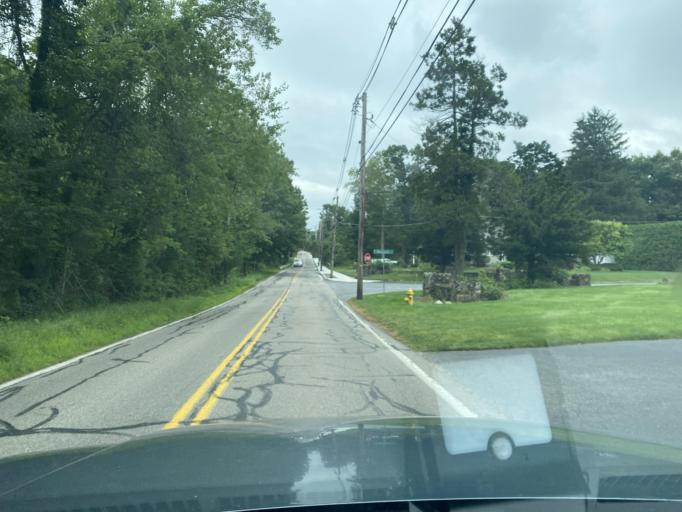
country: US
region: Massachusetts
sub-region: Norfolk County
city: Westwood
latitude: 42.2250
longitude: -71.2292
